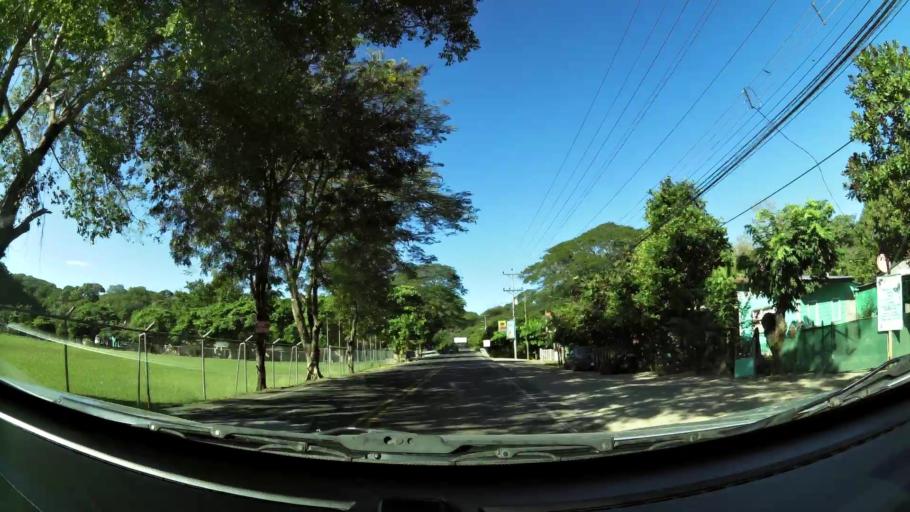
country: CR
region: Guanacaste
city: Belen
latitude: 10.3632
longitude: -85.6477
